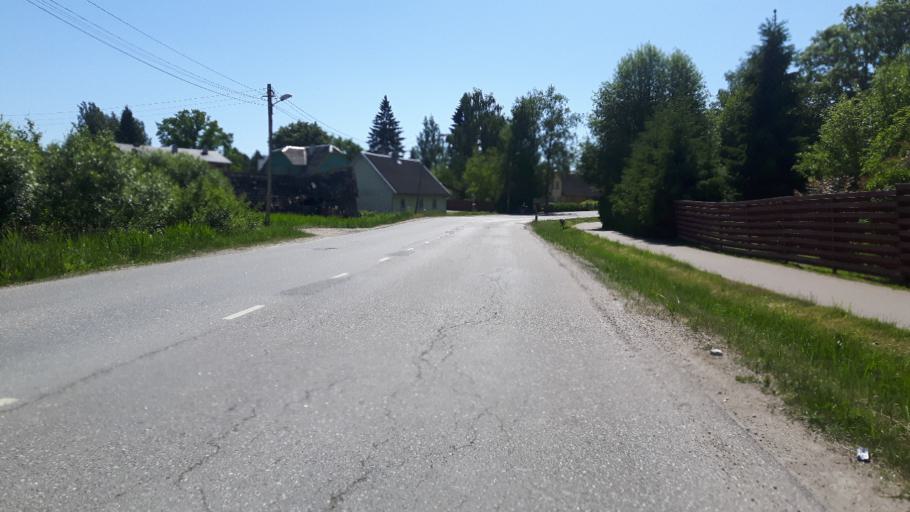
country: EE
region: Paernumaa
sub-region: Sindi linn
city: Sindi
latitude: 58.4115
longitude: 24.6686
